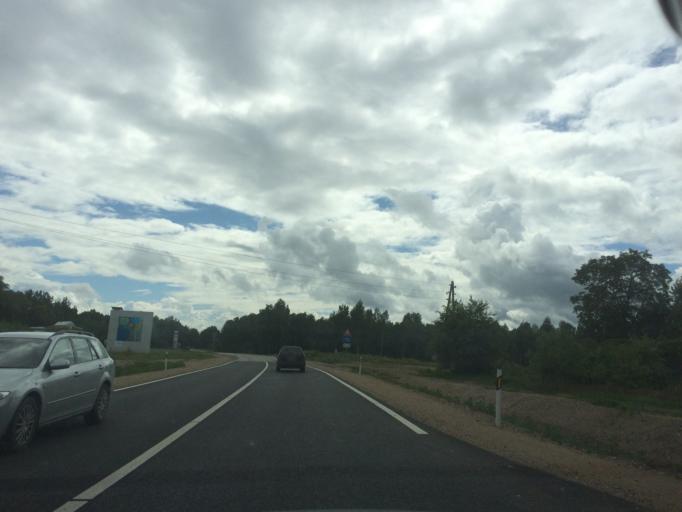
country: LV
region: Rezekne
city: Rezekne
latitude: 56.4905
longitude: 27.3146
